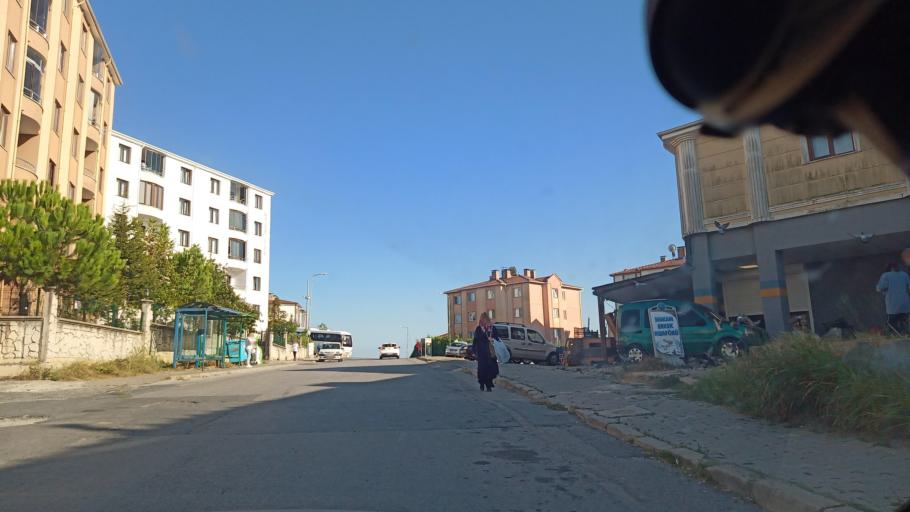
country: TR
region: Sakarya
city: Kazimpasa
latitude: 40.8591
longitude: 30.2891
